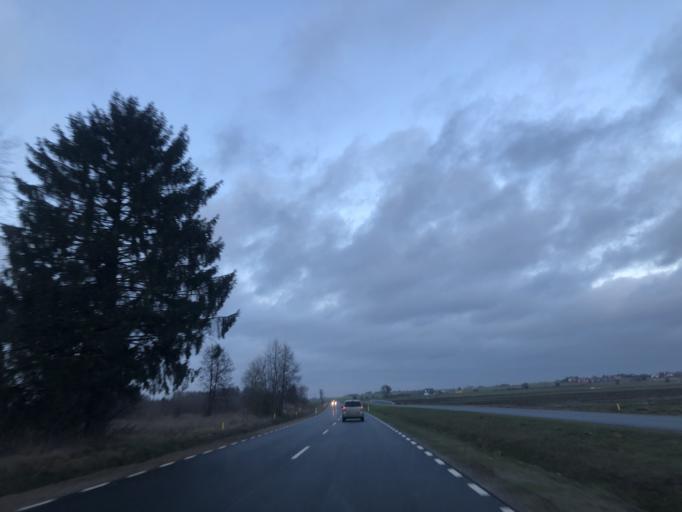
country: PL
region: Podlasie
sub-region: Lomza
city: Lomza
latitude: 53.1317
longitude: 22.0493
